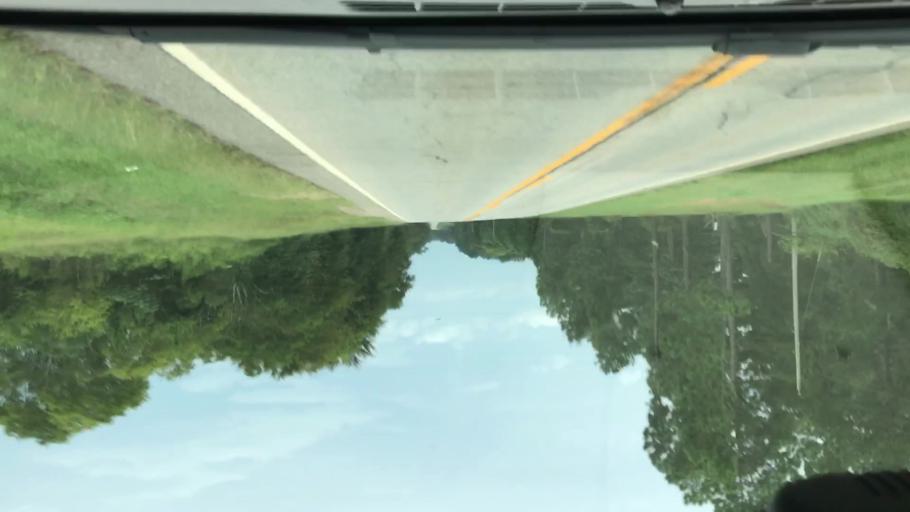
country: US
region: Georgia
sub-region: Early County
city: Blakely
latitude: 31.3277
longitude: -85.0093
